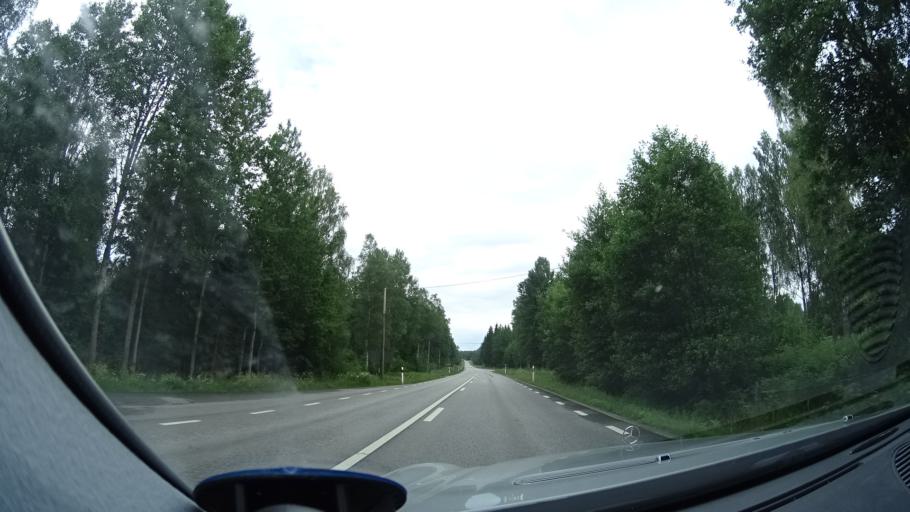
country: SE
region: Kronoberg
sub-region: Tingsryds Kommun
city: Tingsryd
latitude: 56.4803
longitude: 15.0036
